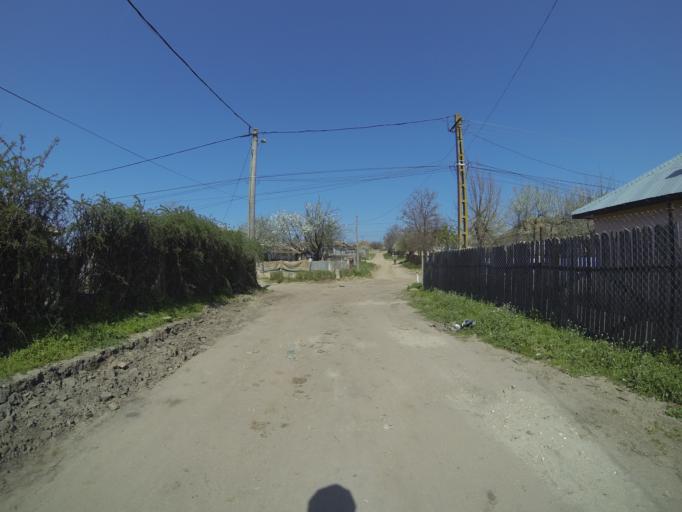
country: RO
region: Dolj
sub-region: Comuna Segarcea
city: Segarcea
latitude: 44.0994
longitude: 23.7309
